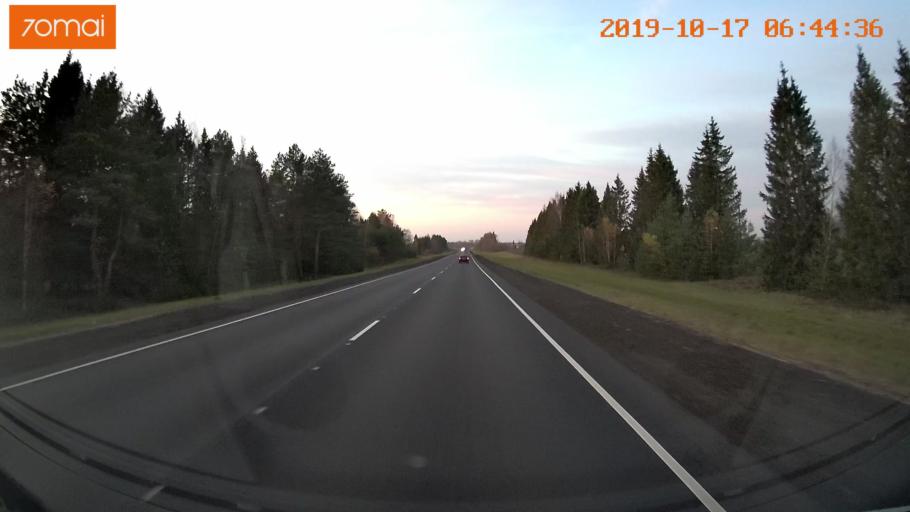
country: RU
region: Vladimir
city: Kideksha
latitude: 56.5700
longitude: 40.5534
